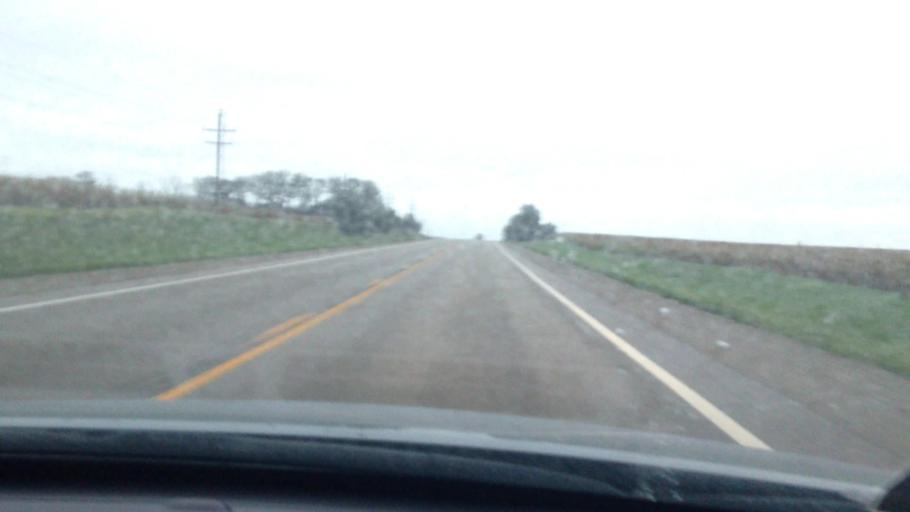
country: US
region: Kansas
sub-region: Brown County
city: Hiawatha
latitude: 39.8192
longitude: -95.5270
